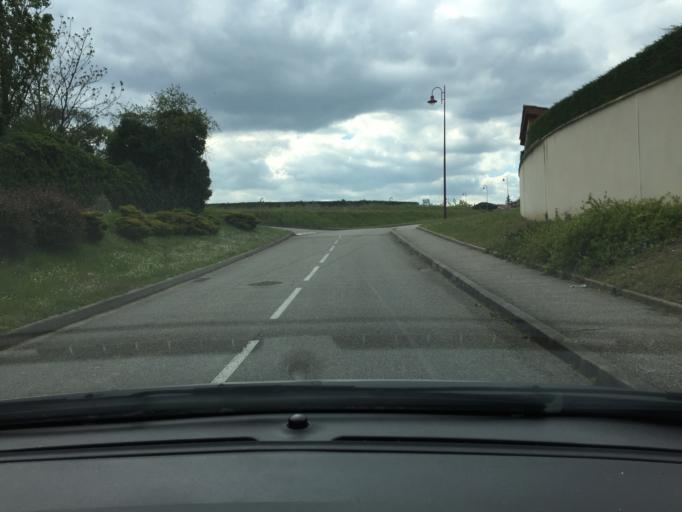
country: FR
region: Rhone-Alpes
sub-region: Departement du Rhone
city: Taluyers
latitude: 45.6365
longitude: 4.7251
